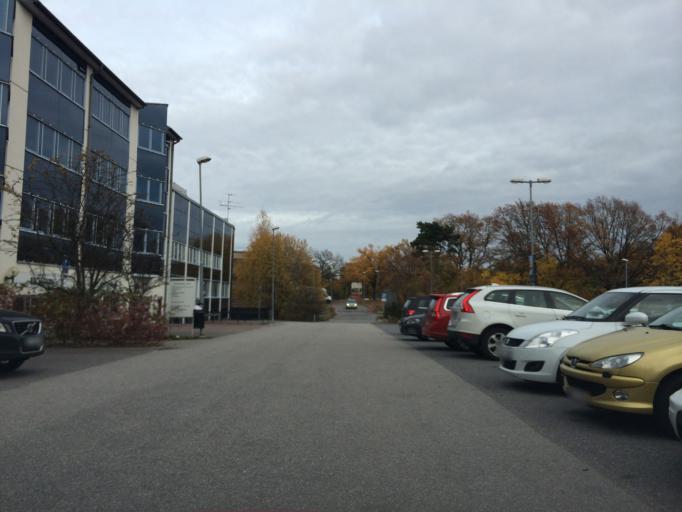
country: SE
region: Stockholm
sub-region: Sundbybergs Kommun
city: Sundbyberg
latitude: 59.3458
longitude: 17.9598
